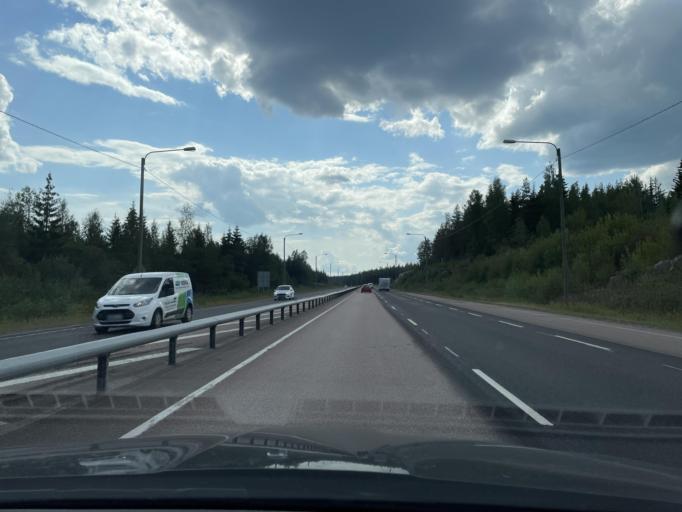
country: FI
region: Central Finland
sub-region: Jyvaeskylae
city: Muurame
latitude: 62.0900
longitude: 25.6189
